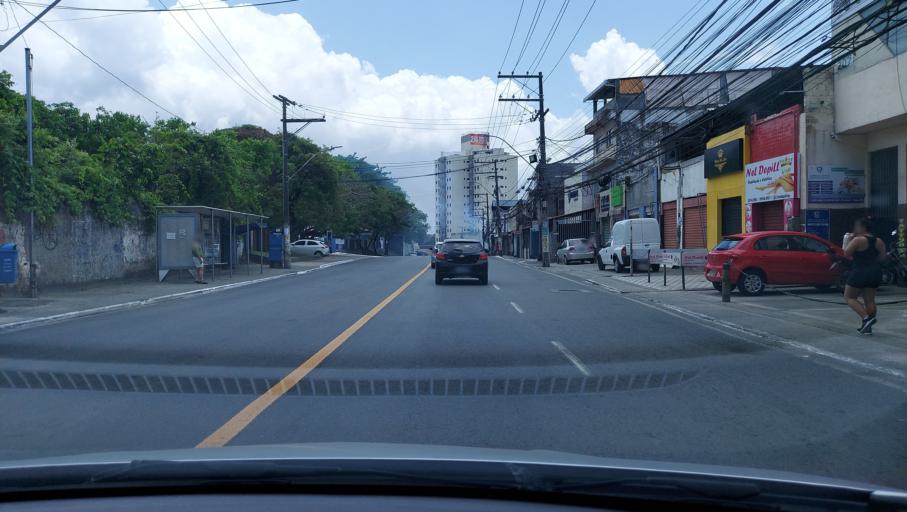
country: BR
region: Bahia
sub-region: Salvador
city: Salvador
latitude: -12.9593
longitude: -38.4675
